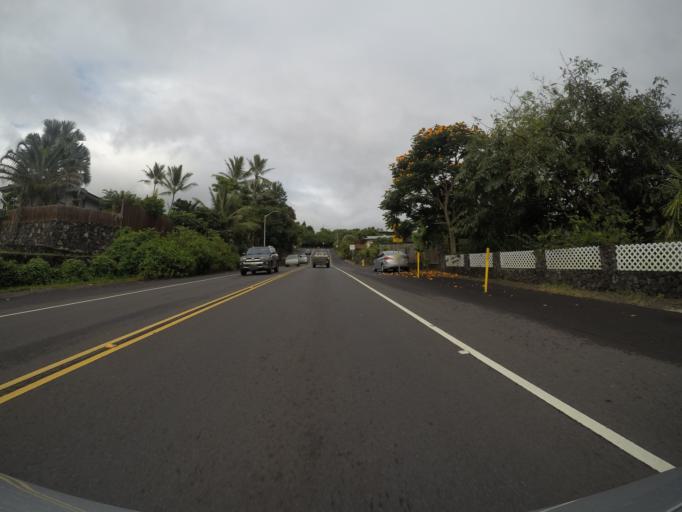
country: US
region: Hawaii
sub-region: Hawaii County
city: Kalaoa
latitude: 19.7176
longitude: -155.9792
